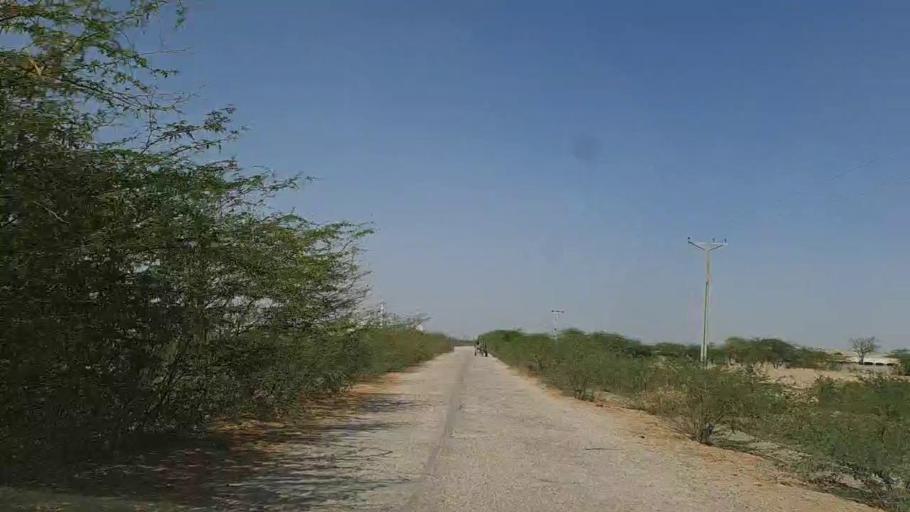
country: PK
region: Sindh
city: Naukot
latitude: 24.6373
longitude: 69.2881
